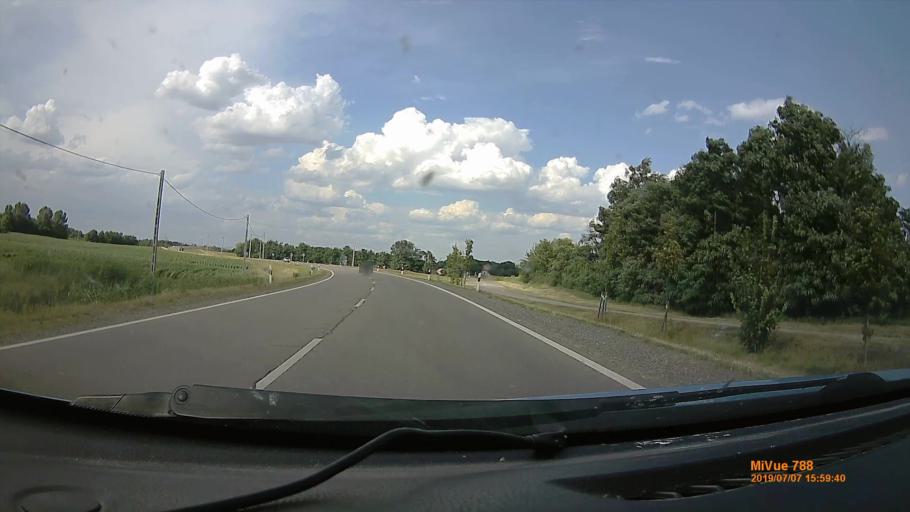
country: HU
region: Heves
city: Boldog
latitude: 47.5892
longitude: 19.7487
